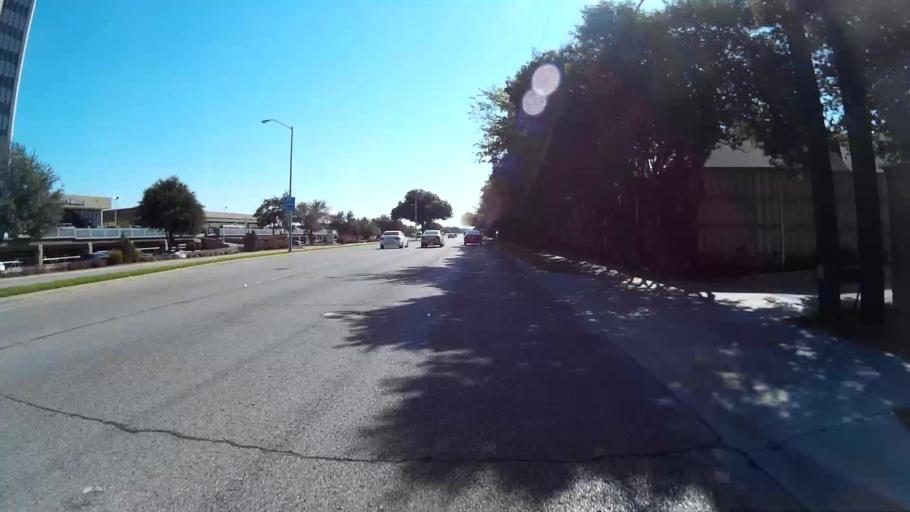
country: US
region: Texas
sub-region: Dallas County
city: Richardson
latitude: 32.9555
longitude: -96.7690
